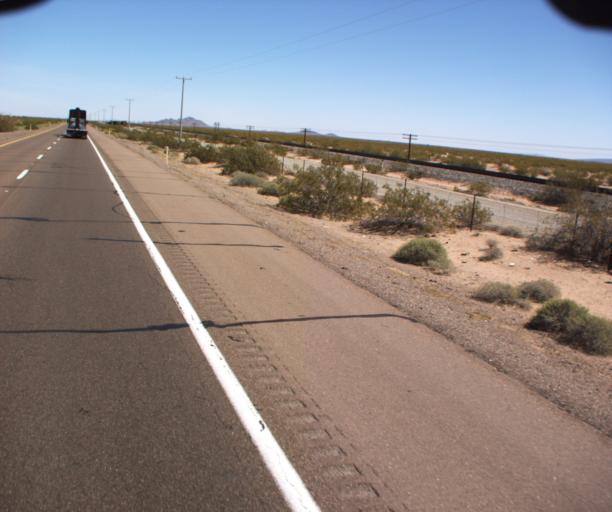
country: US
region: Arizona
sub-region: Yuma County
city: Wellton
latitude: 32.7653
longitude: -113.6226
